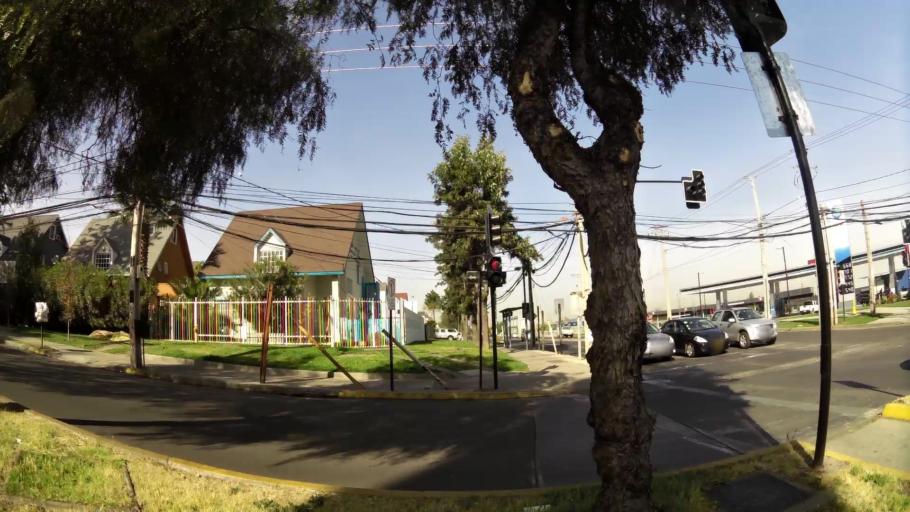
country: CL
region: Santiago Metropolitan
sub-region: Provincia de Santiago
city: Villa Presidente Frei, Nunoa, Santiago, Chile
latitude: -33.4835
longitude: -70.5466
